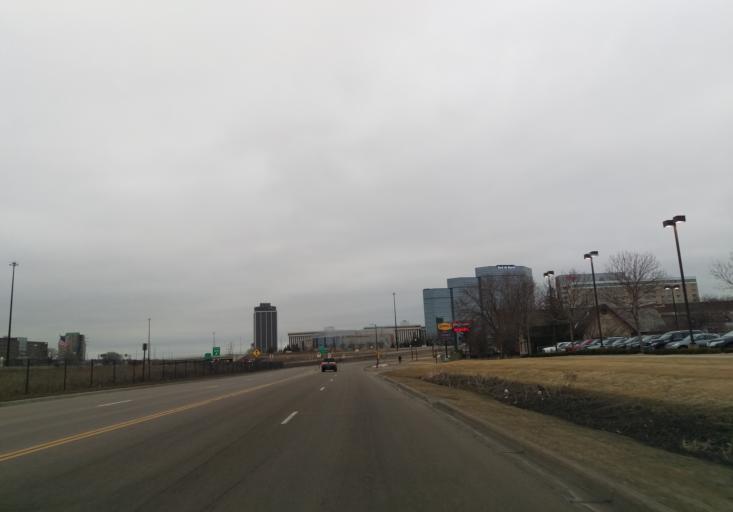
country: US
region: Minnesota
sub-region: Hennepin County
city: Edina
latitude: 44.8576
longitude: -93.3346
